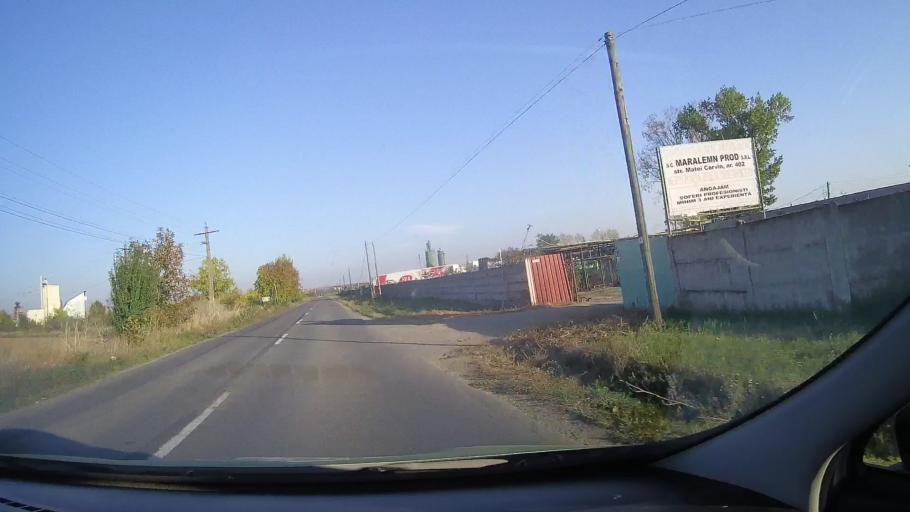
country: RO
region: Bihor
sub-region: Comuna Bors
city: Santion
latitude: 47.1134
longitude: 21.8524
